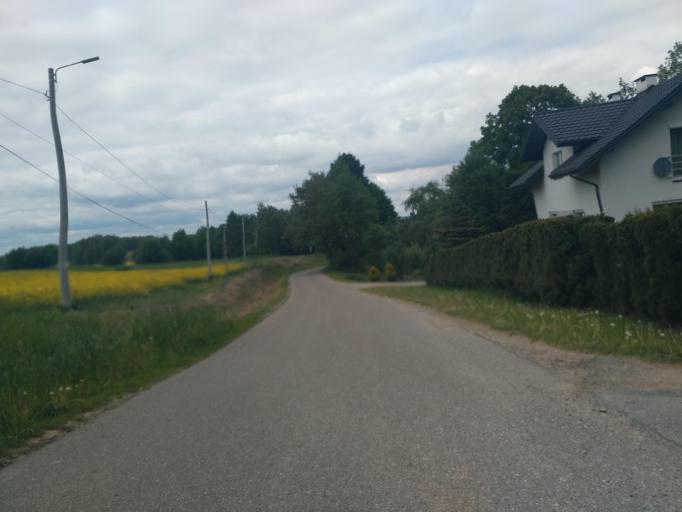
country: PL
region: Subcarpathian Voivodeship
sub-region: Powiat jasielski
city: Tarnowiec
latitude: 49.6972
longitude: 21.5812
